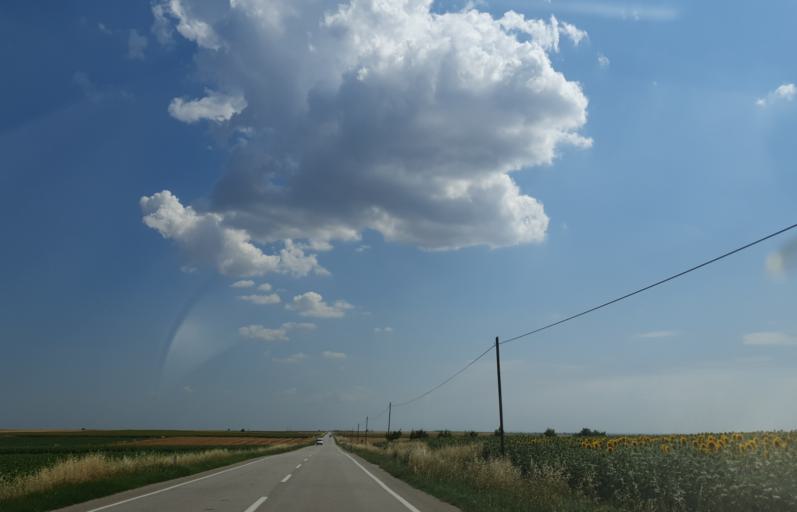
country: TR
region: Kirklareli
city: Buyukkaristiran
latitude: 41.4249
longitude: 27.5809
